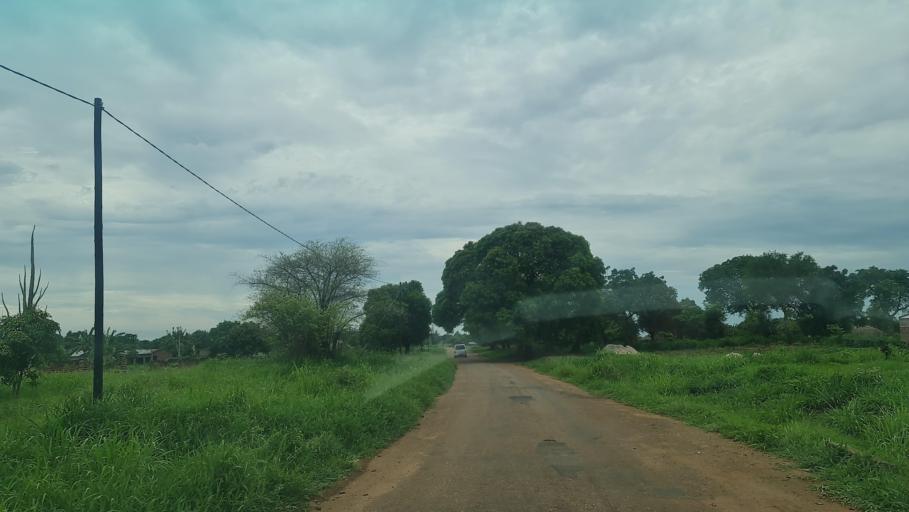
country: MW
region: Southern Region
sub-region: Nsanje District
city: Nsanje
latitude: -17.6716
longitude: 35.7152
